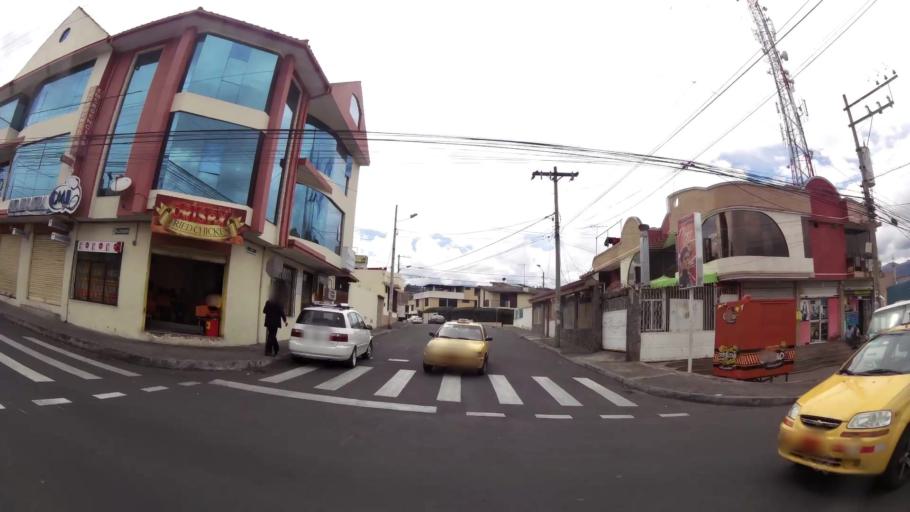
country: EC
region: Tungurahua
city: Ambato
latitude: -1.2717
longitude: -78.6266
